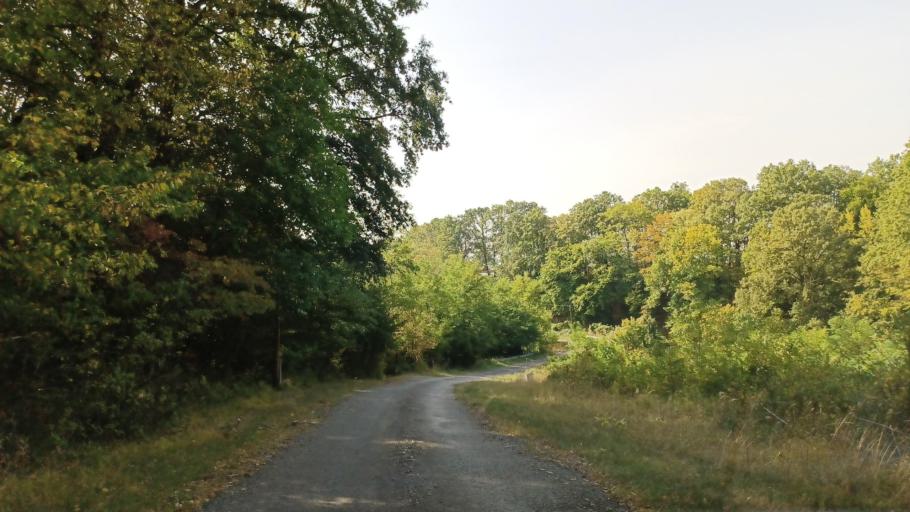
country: HU
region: Baranya
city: Mecseknadasd
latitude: 46.1931
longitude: 18.4494
